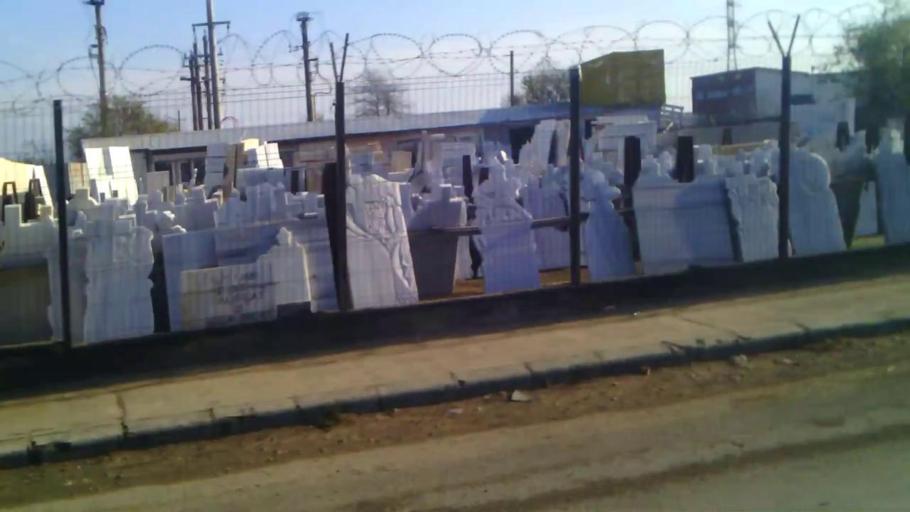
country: RO
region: Ilfov
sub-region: Comuna Berceni
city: Berceni
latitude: 44.3418
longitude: 26.1639
